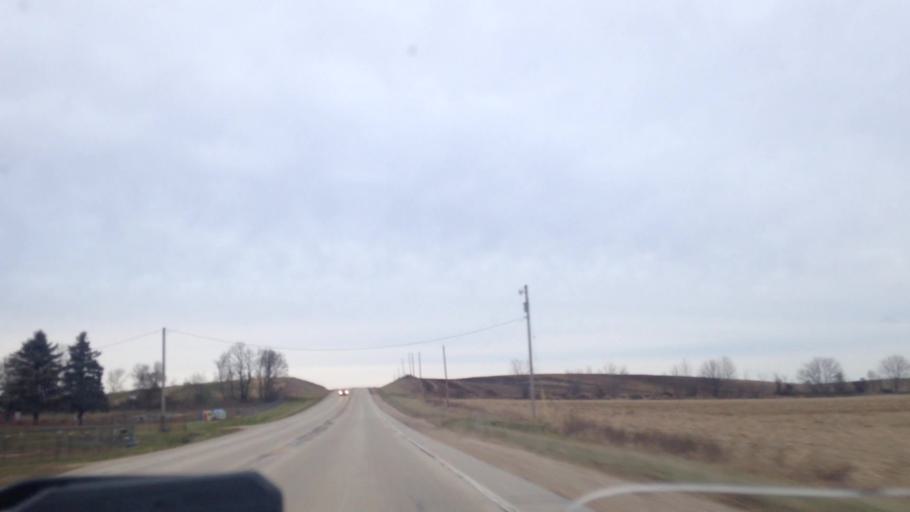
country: US
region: Wisconsin
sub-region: Dodge County
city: Theresa
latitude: 43.4767
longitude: -88.4501
